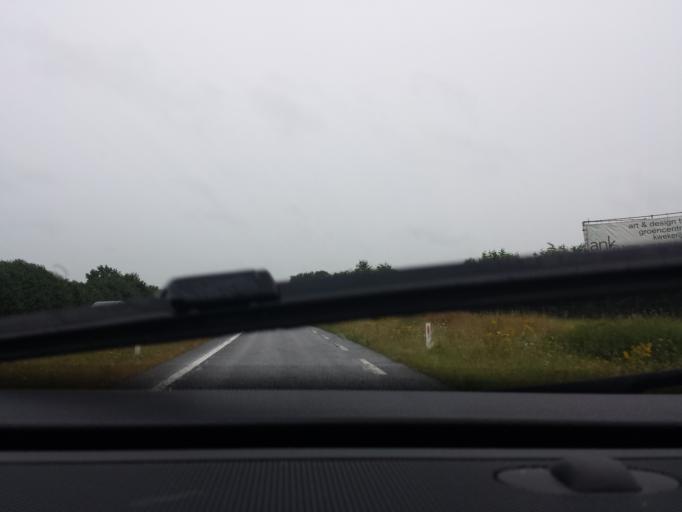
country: NL
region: Gelderland
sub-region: Gemeente Montferland
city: s-Heerenberg
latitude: 51.9107
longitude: 6.2660
